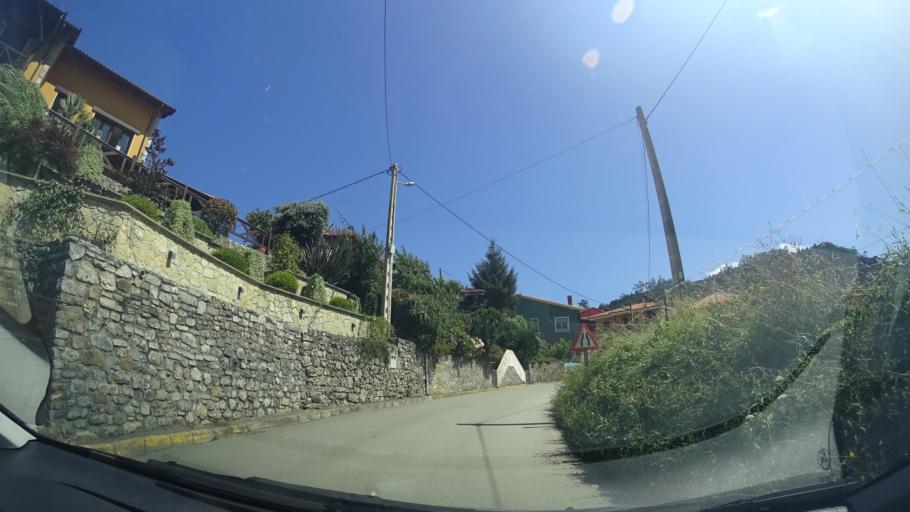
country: ES
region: Asturias
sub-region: Province of Asturias
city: Ribadesella
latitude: 43.4780
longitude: -5.1315
